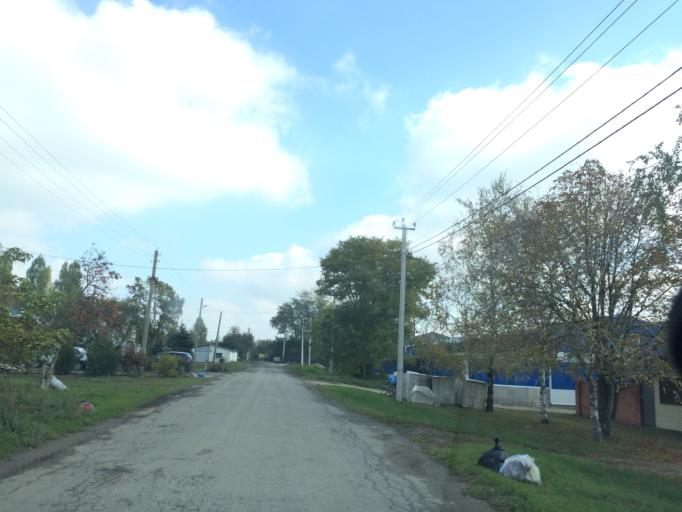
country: RU
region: Rostov
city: Aksay
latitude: 47.3042
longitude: 39.8337
